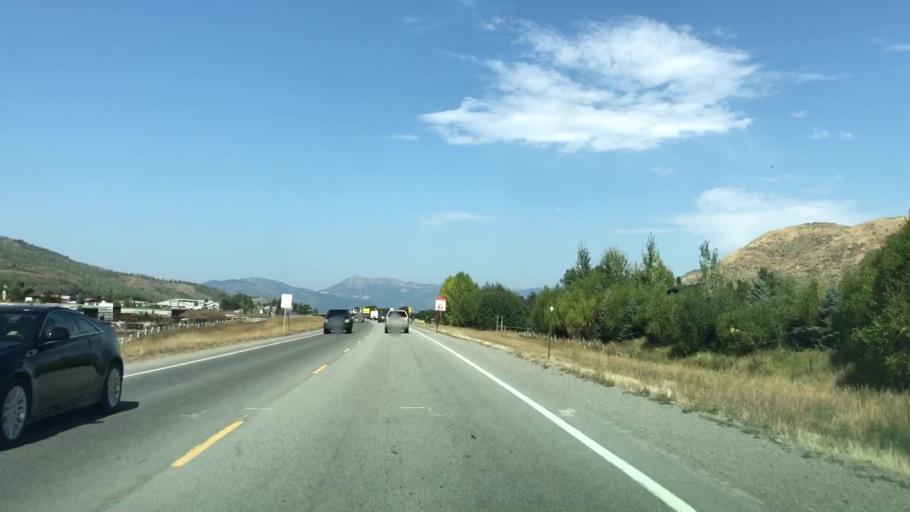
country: US
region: Wyoming
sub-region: Teton County
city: South Park
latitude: 43.3675
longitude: -110.7346
